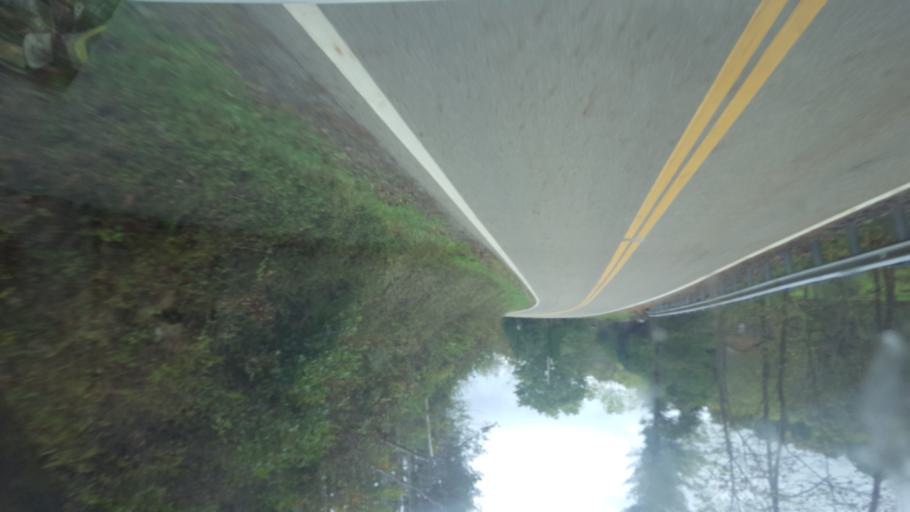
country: US
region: Ohio
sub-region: Knox County
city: Danville
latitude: 40.5197
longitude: -82.1102
